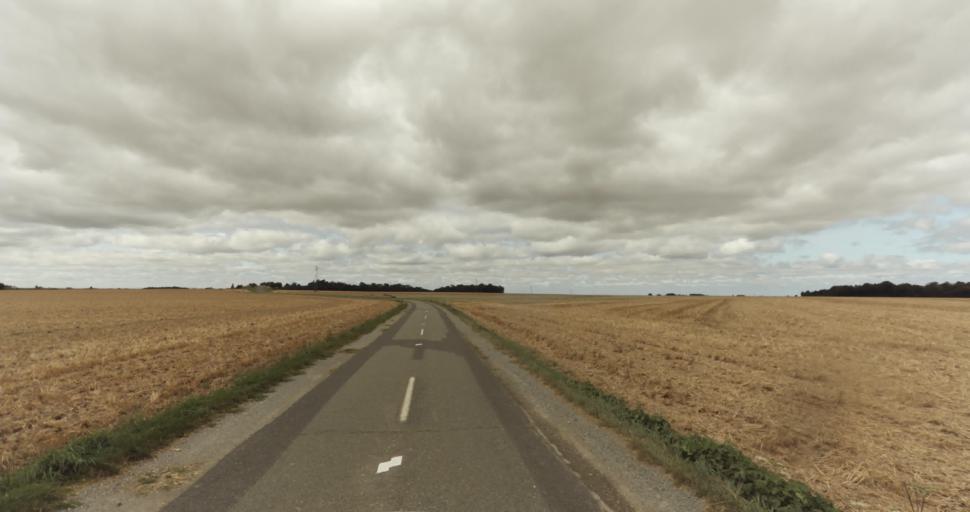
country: FR
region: Haute-Normandie
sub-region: Departement de l'Eure
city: Evreux
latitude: 48.9352
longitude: 1.2178
